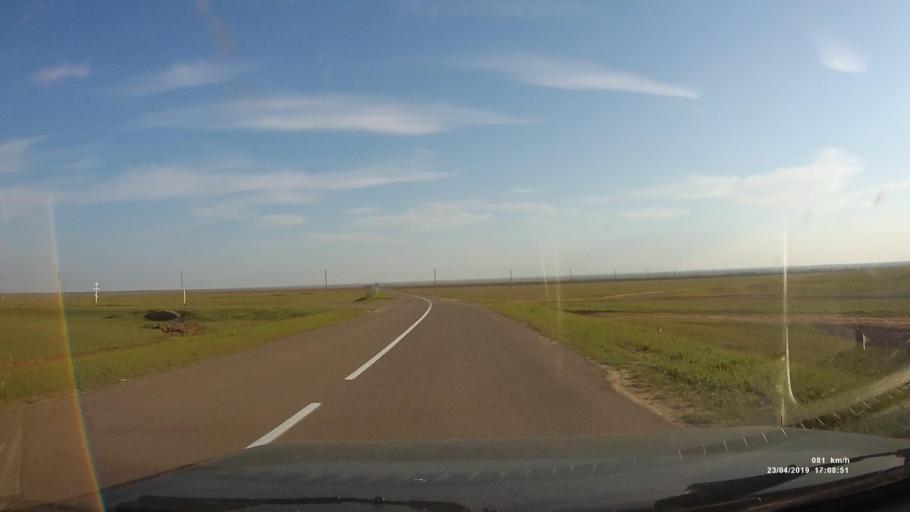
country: RU
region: Kalmykiya
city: Priyutnoye
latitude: 46.2664
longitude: 43.4845
